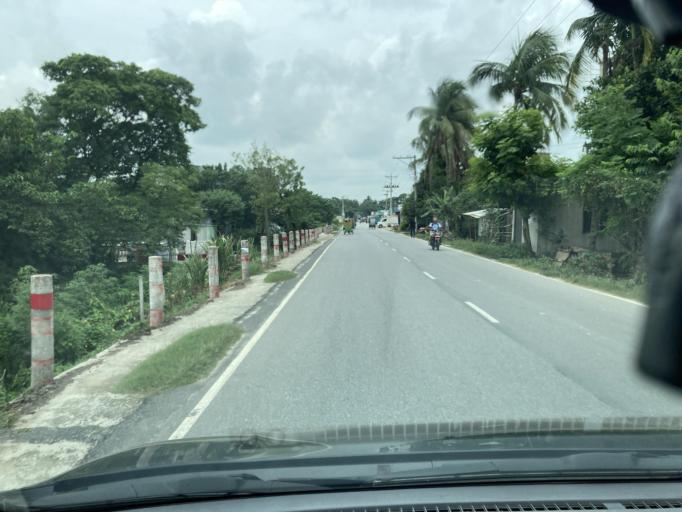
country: BD
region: Dhaka
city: Azimpur
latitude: 23.8059
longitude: 90.2102
